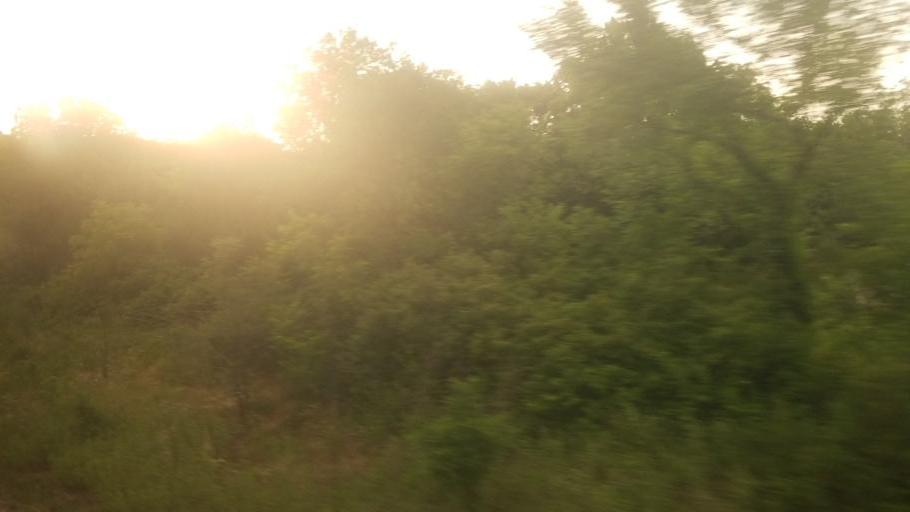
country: US
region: Kansas
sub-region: Lyon County
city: Emporia
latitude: 38.4349
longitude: -96.1177
